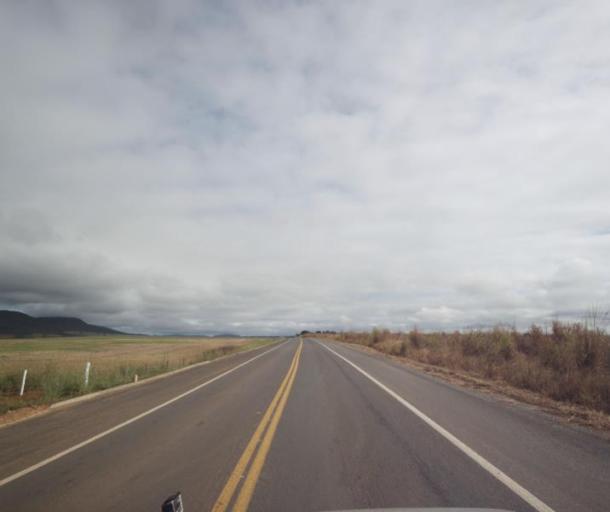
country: BR
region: Goias
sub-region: Padre Bernardo
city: Padre Bernardo
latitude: -15.3889
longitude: -48.6389
